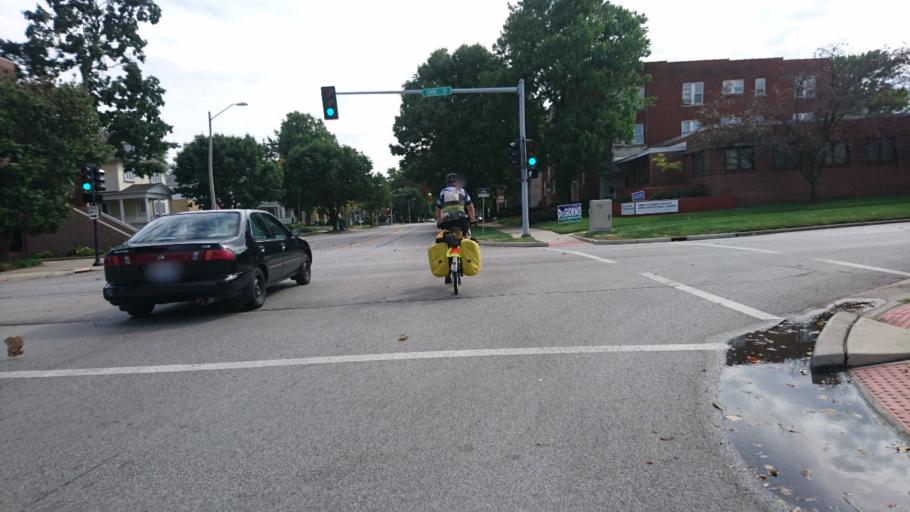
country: US
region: Illinois
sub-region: Sangamon County
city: Springfield
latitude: 39.7952
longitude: -89.6535
